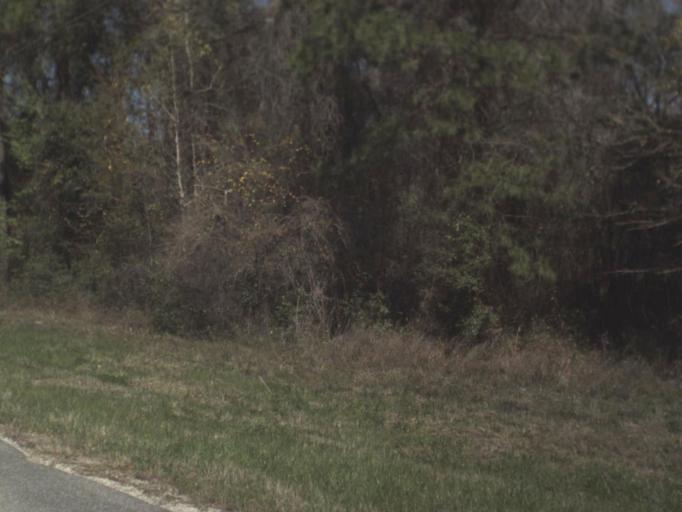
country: US
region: Florida
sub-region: Leon County
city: Woodville
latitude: 30.2443
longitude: -84.2326
